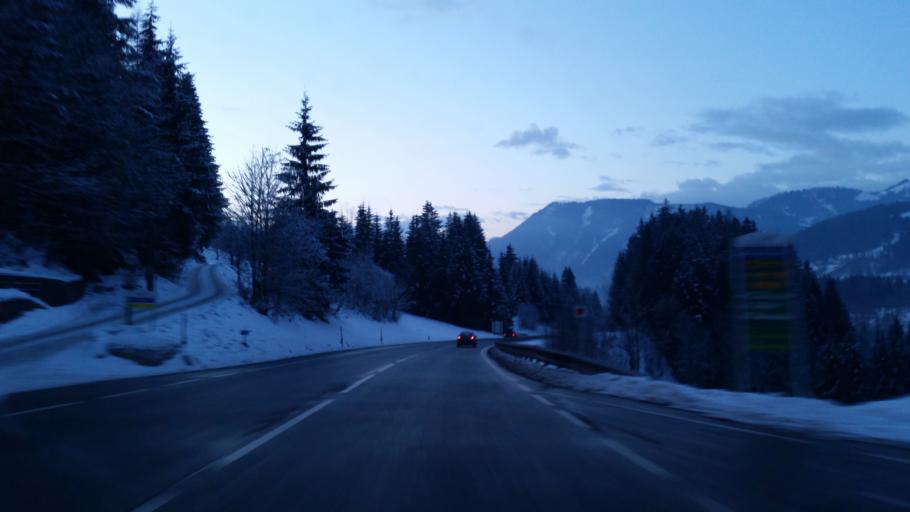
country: AT
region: Salzburg
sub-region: Politischer Bezirk Sankt Johann im Pongau
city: Eben im Pongau
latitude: 47.4156
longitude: 13.3845
